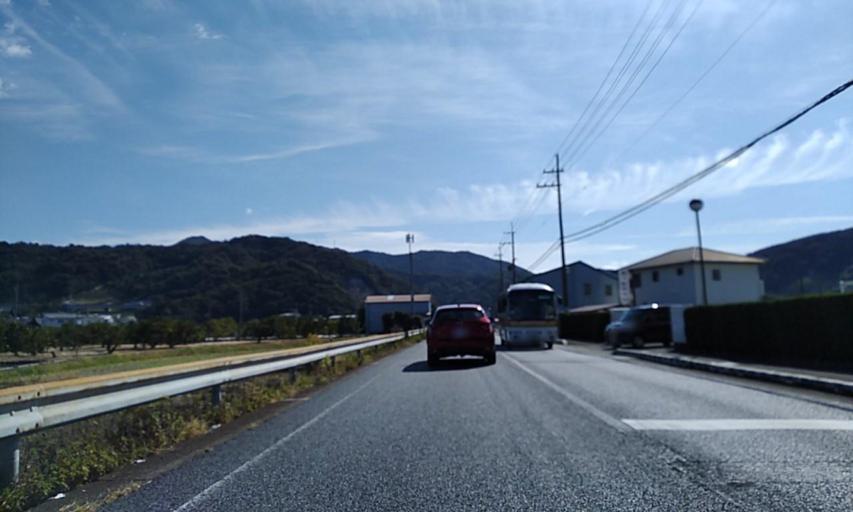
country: JP
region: Wakayama
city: Kainan
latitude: 34.0188
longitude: 135.1824
